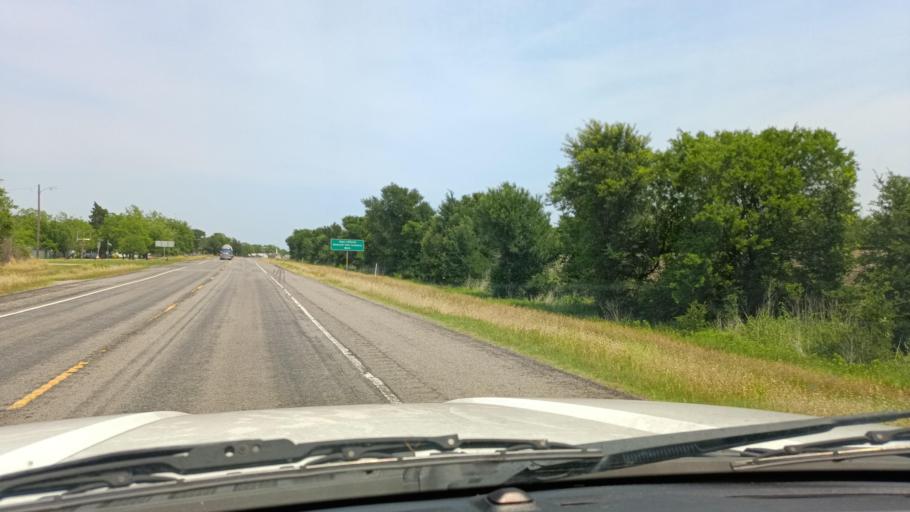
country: US
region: Texas
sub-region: Bell County
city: Rogers
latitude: 30.8755
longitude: -97.1322
